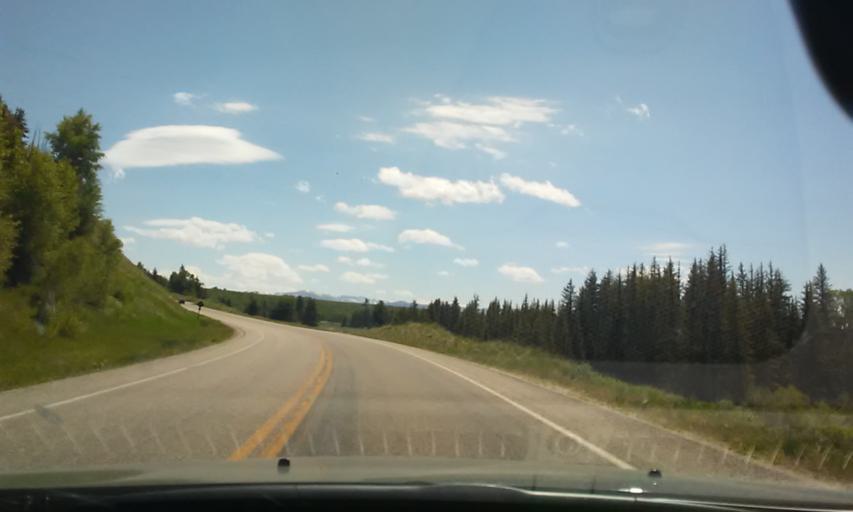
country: US
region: Wyoming
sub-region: Teton County
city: Jackson
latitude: 43.8373
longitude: -110.5006
